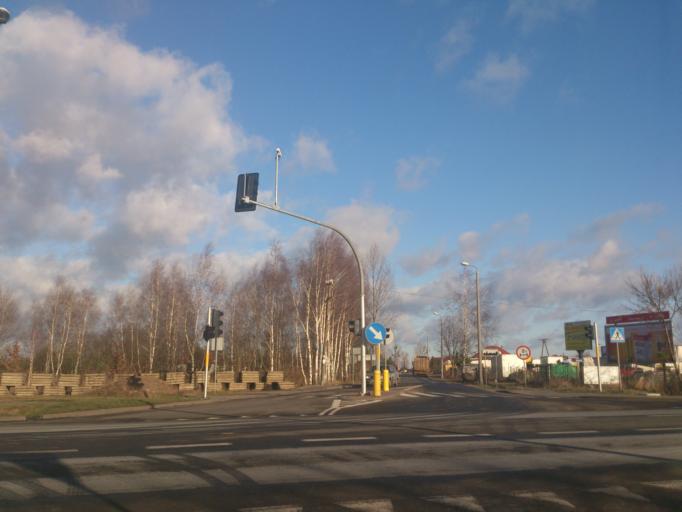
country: PL
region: Kujawsko-Pomorskie
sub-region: Powiat torunski
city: Lubicz Gorny
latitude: 53.0205
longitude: 18.8009
